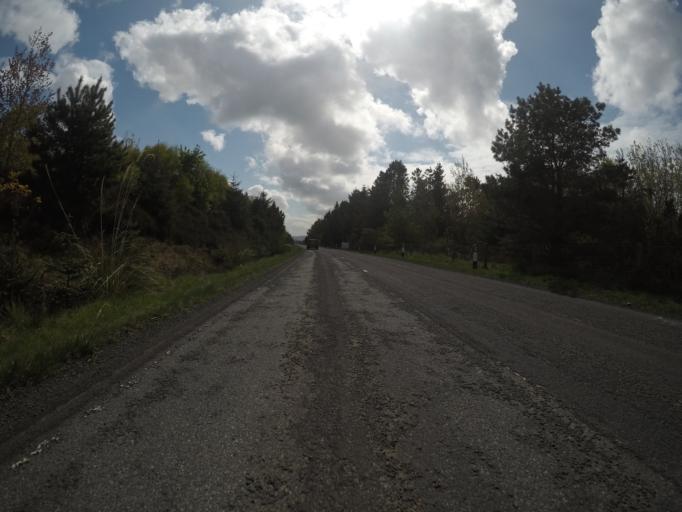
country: GB
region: Scotland
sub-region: Highland
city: Portree
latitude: 57.5702
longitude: -6.3644
